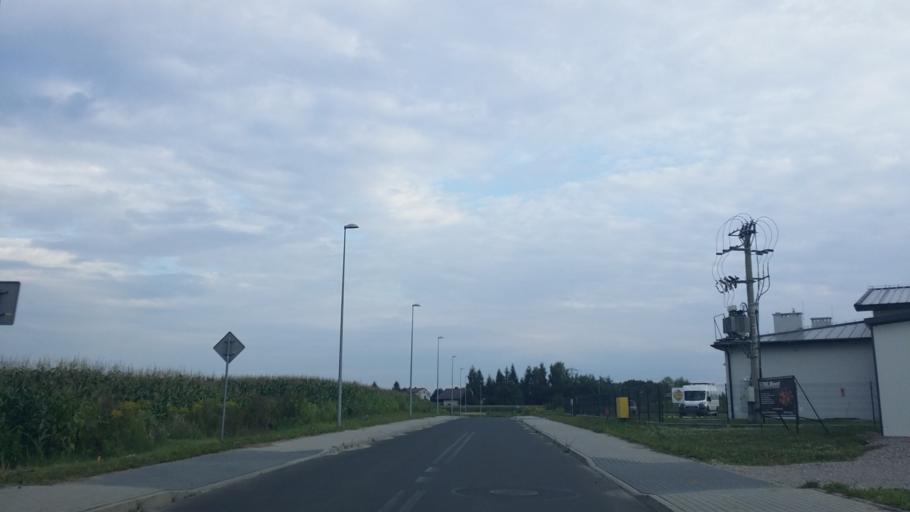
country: PL
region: Lesser Poland Voivodeship
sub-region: Powiat oswiecimski
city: Zator
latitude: 49.9940
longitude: 19.4256
